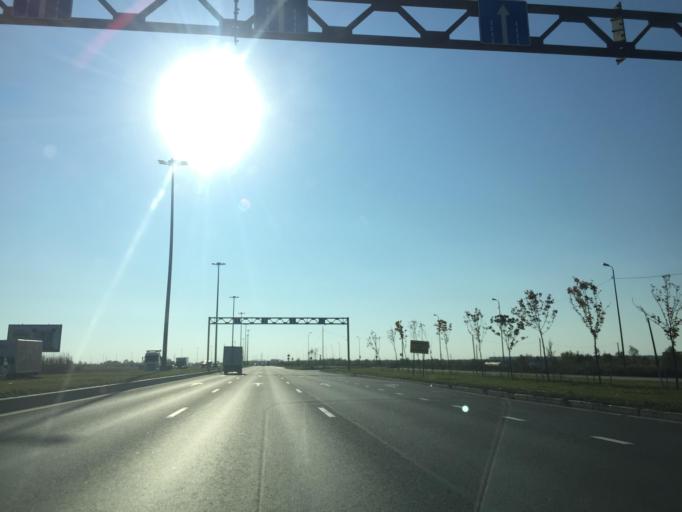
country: RU
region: St.-Petersburg
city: Petro-Slavyanka
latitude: 59.7723
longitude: 30.4996
